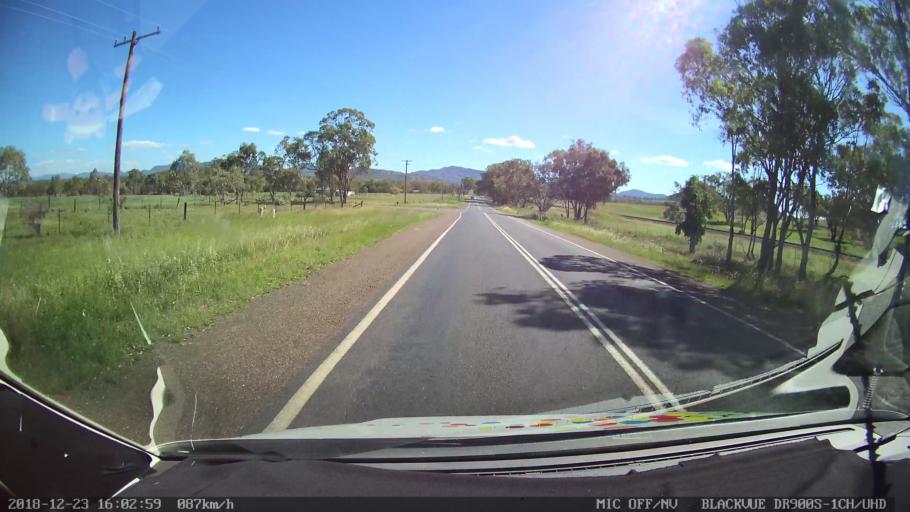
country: AU
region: New South Wales
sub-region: Tamworth Municipality
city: Phillip
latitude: -31.2383
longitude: 150.8046
